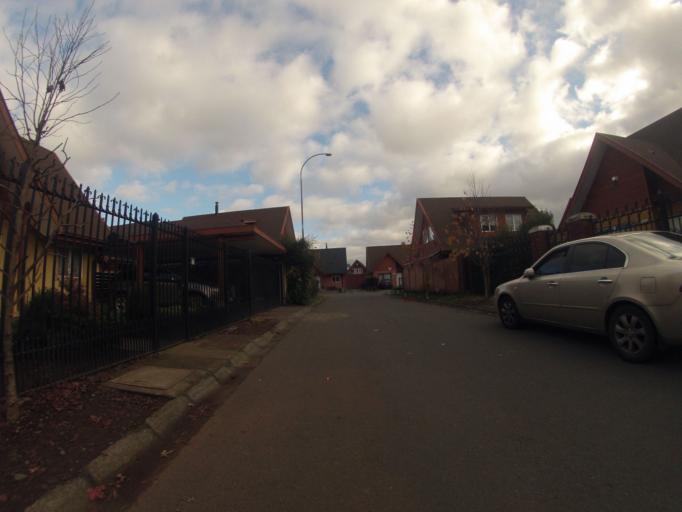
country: CL
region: Araucania
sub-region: Provincia de Cautin
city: Temuco
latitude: -38.7389
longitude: -72.6453
